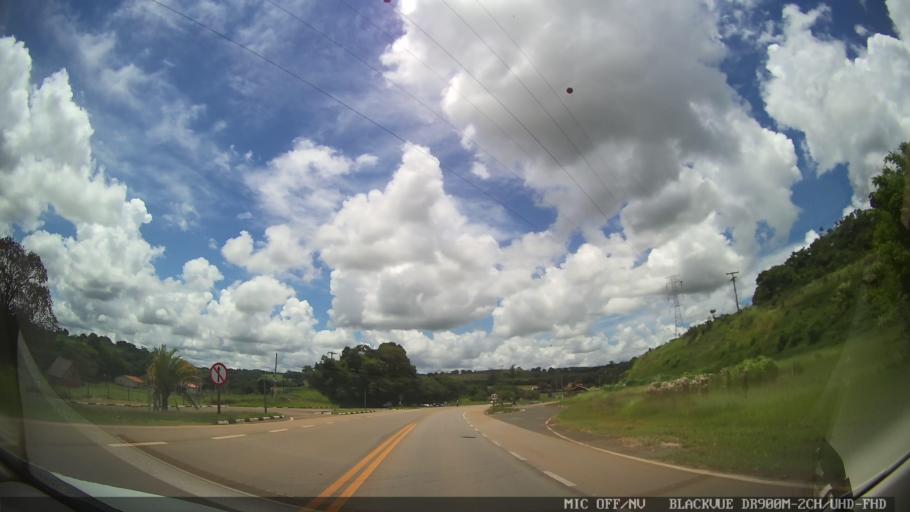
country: BR
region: Sao Paulo
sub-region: Amparo
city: Amparo
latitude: -22.8067
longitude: -46.6995
